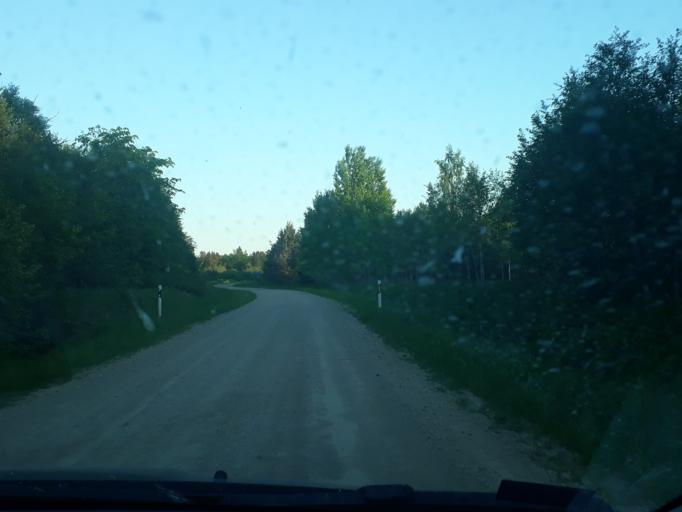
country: EE
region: Paernumaa
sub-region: Vaendra vald (alev)
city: Vandra
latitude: 58.5637
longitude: 24.9519
